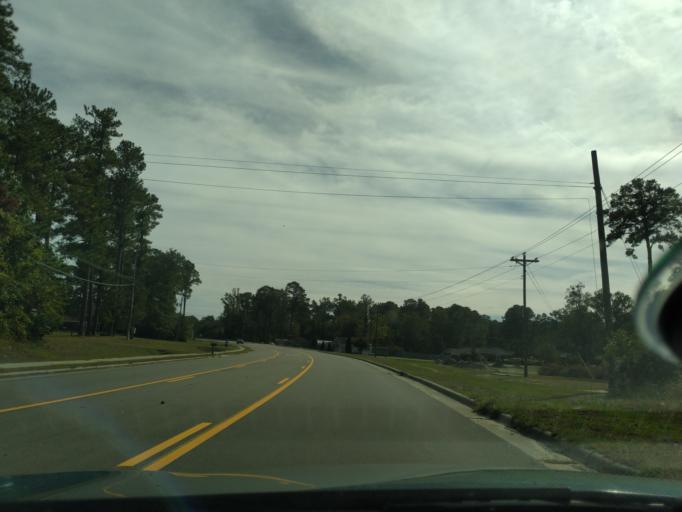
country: US
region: North Carolina
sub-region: Beaufort County
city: River Road
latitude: 35.5167
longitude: -77.0047
